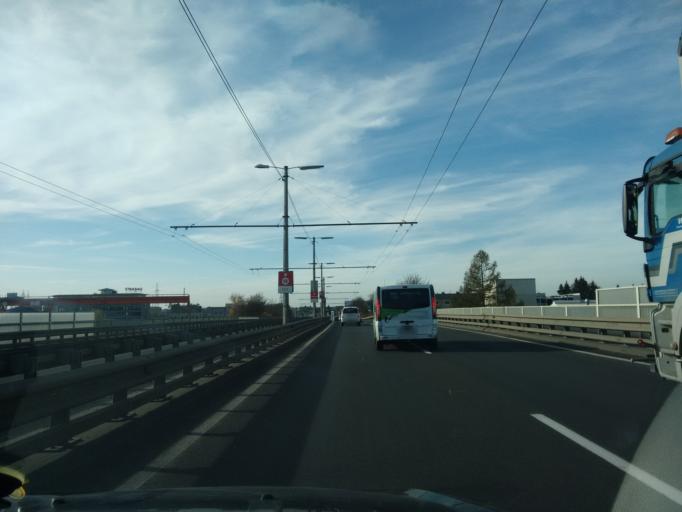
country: AT
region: Upper Austria
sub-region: Politischer Bezirk Linz-Land
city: Leonding
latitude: 48.2523
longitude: 14.2764
